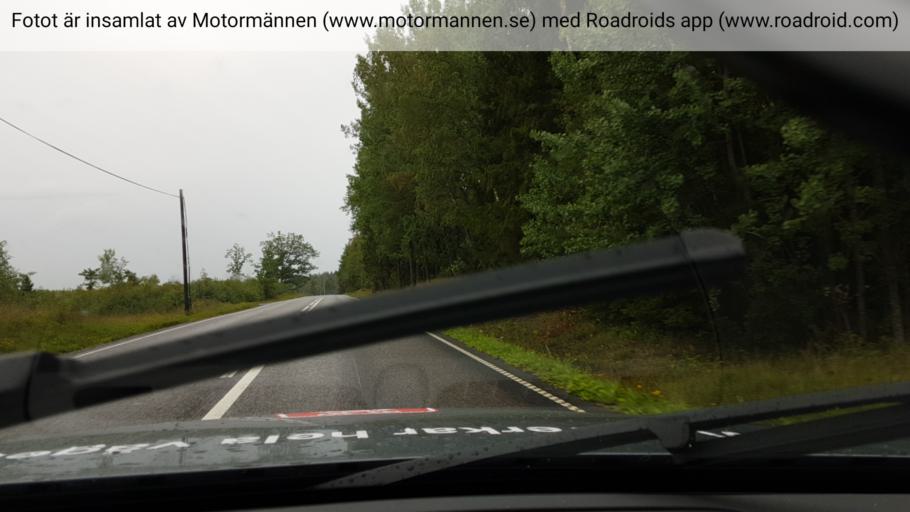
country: SE
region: Soedermanland
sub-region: Eskilstuna Kommun
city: Eskilstuna
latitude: 59.3261
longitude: 16.5301
